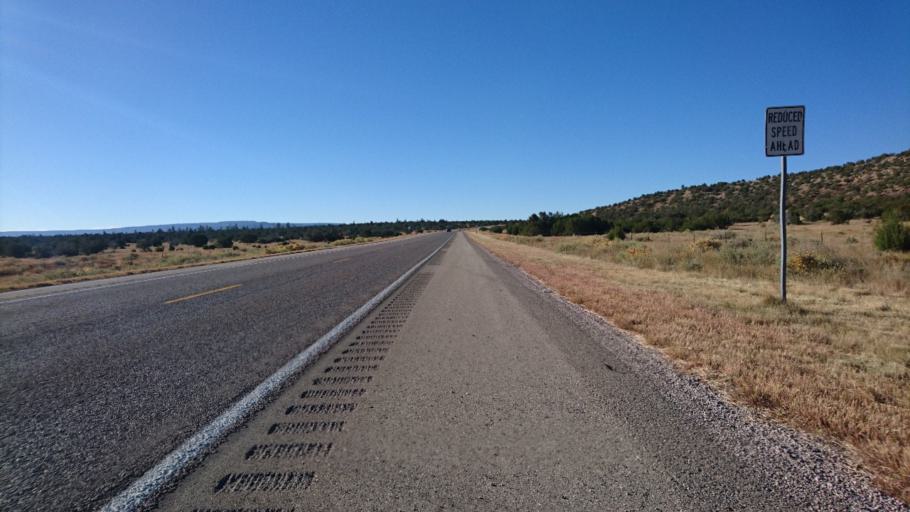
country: US
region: New Mexico
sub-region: Cibola County
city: Grants
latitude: 34.9704
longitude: -107.9126
